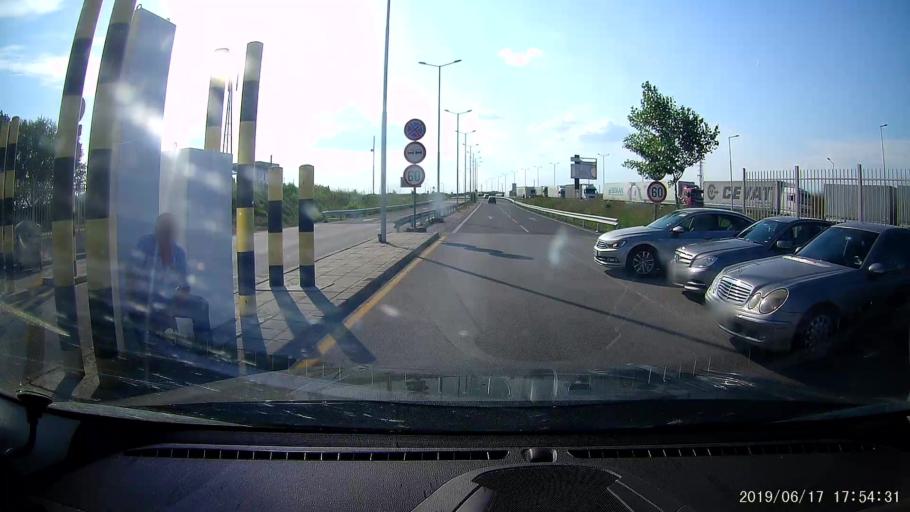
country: GR
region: East Macedonia and Thrace
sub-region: Nomos Evrou
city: Rizia
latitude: 41.7190
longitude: 26.3452
